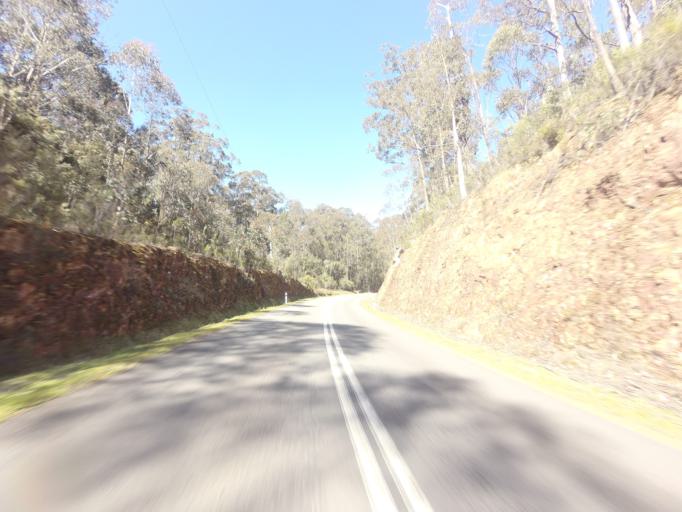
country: AU
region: Tasmania
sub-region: Derwent Valley
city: New Norfolk
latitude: -42.7373
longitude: 146.4940
